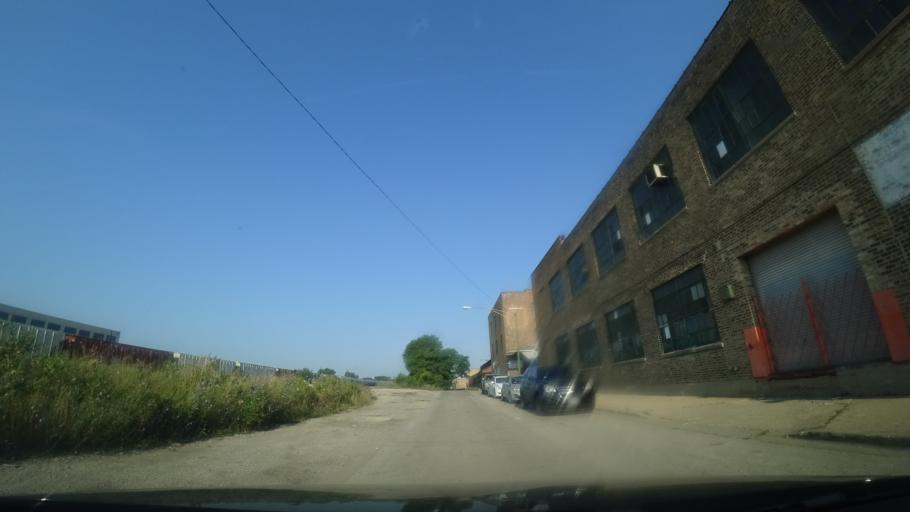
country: US
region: Illinois
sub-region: Cook County
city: Oak Park
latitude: 41.9169
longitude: -87.7684
